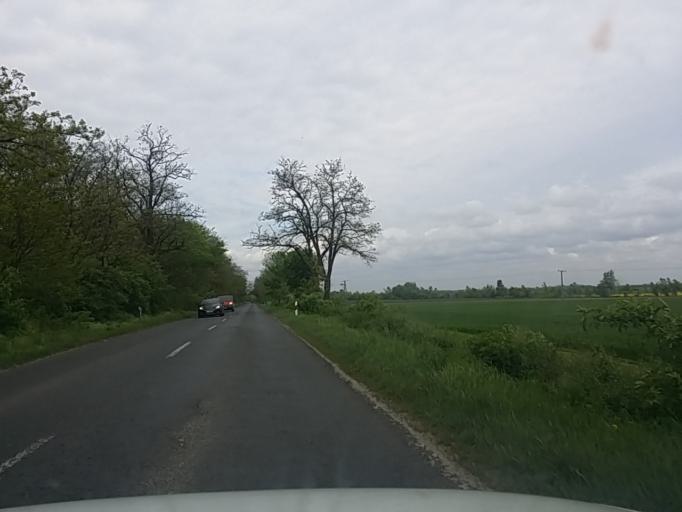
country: HU
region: Pest
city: Forropuszta
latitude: 47.4532
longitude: 19.6748
